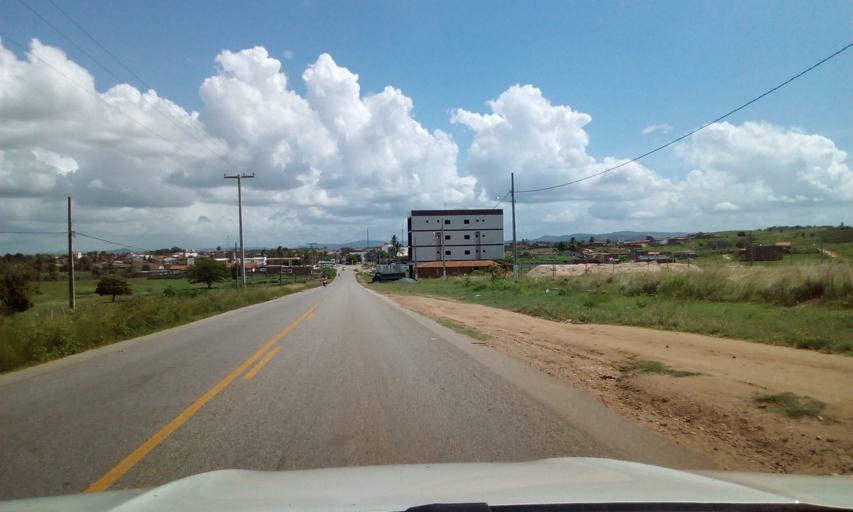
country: BR
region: Paraiba
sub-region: Guarabira
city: Guarabira
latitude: -6.8498
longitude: -35.3706
